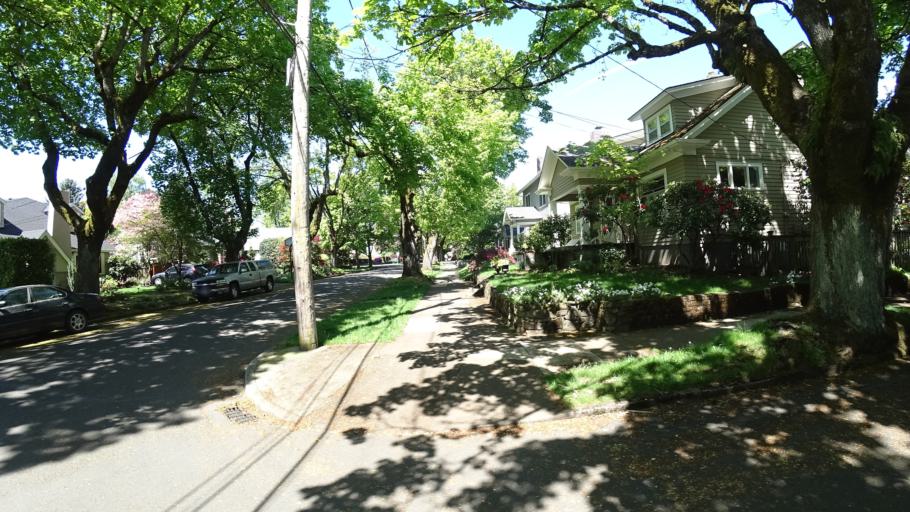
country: US
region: Oregon
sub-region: Clackamas County
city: Milwaukie
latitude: 45.4664
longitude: -122.6262
